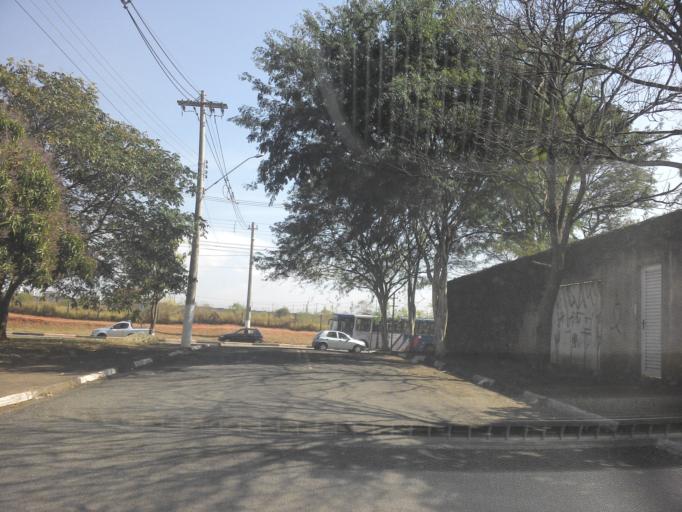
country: BR
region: Sao Paulo
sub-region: Hortolandia
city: Hortolandia
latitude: -22.8736
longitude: -47.2275
